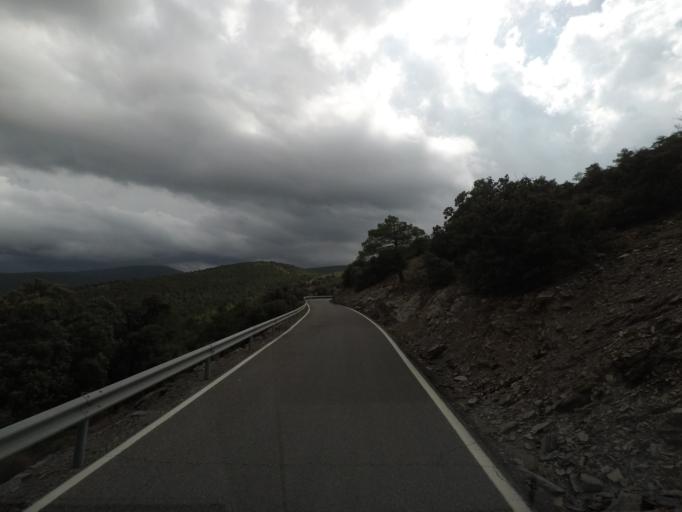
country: ES
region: Andalusia
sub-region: Provincia de Granada
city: Ferreira
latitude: 37.1543
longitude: -3.0494
